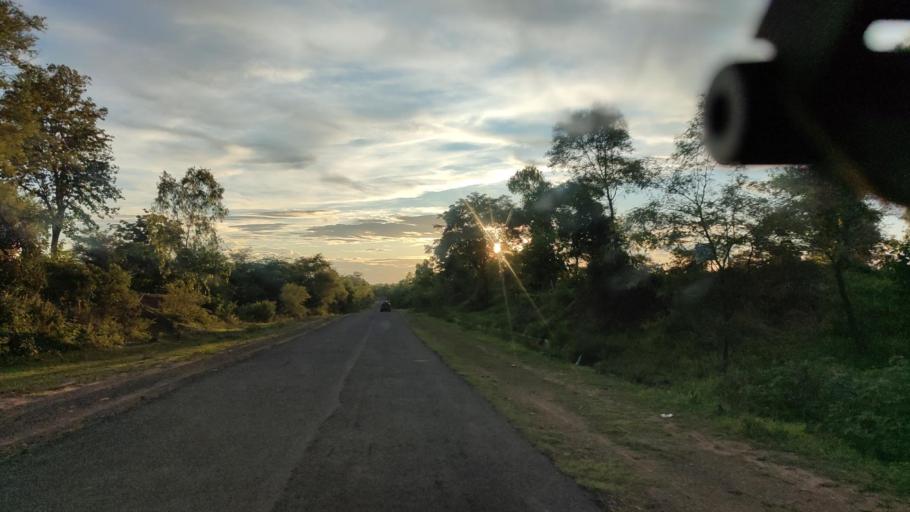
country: MM
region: Magway
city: Taungdwingyi
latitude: 20.1416
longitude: 95.6512
